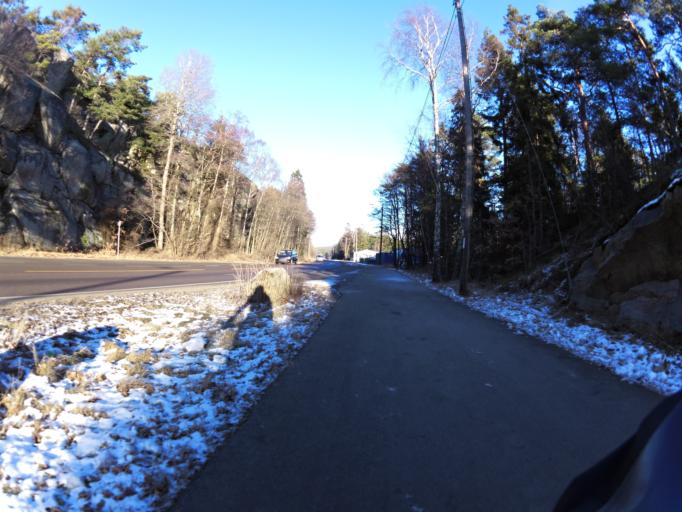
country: NO
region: Ostfold
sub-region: Fredrikstad
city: Fredrikstad
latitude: 59.1868
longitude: 10.8483
